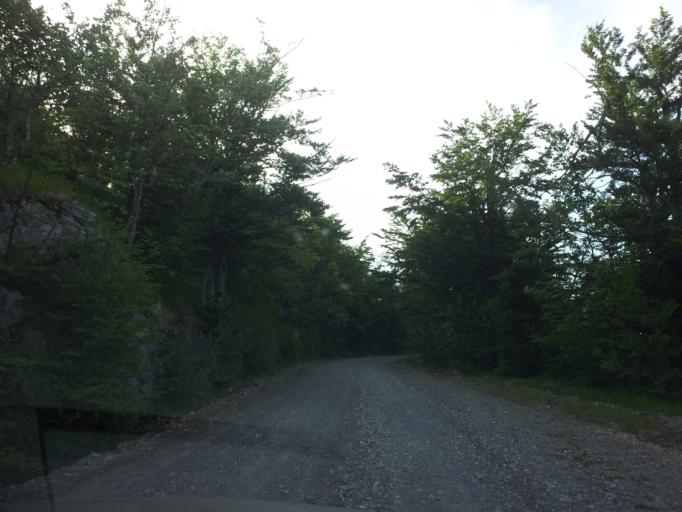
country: HR
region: Zadarska
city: Obrovac
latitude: 44.2970
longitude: 15.6670
